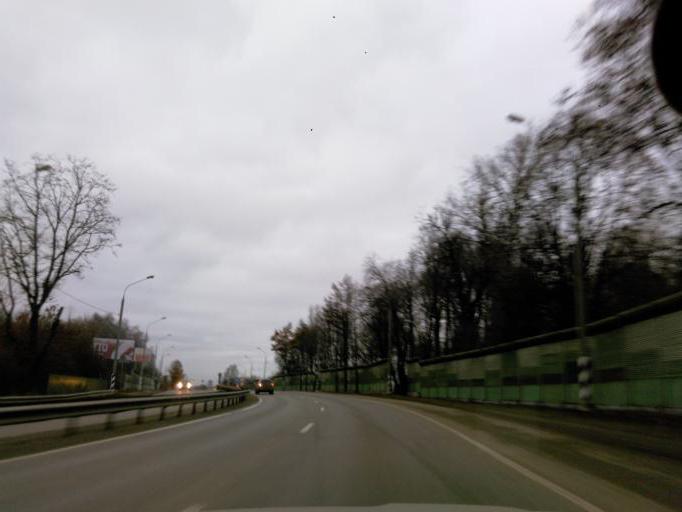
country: RU
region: Moskovskaya
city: Chashnikovo
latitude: 56.0347
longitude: 37.1643
